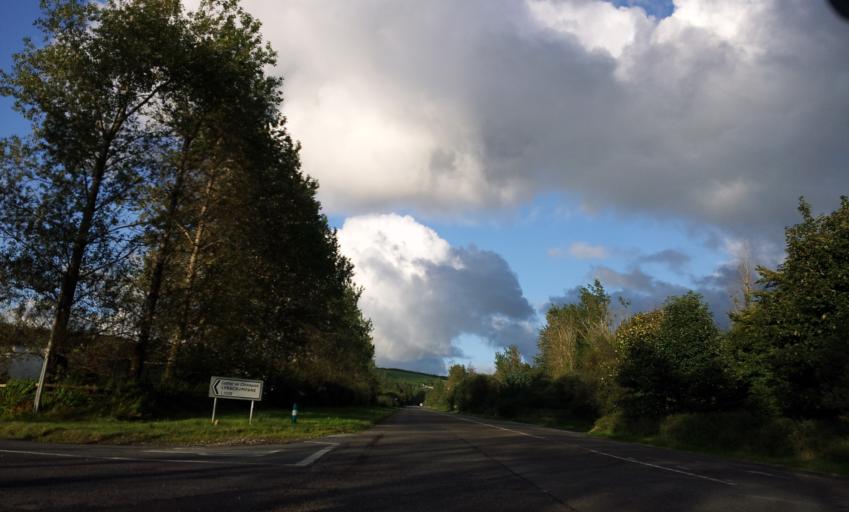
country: IE
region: Munster
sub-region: Ciarrai
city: Castleisland
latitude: 52.2632
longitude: -9.4543
